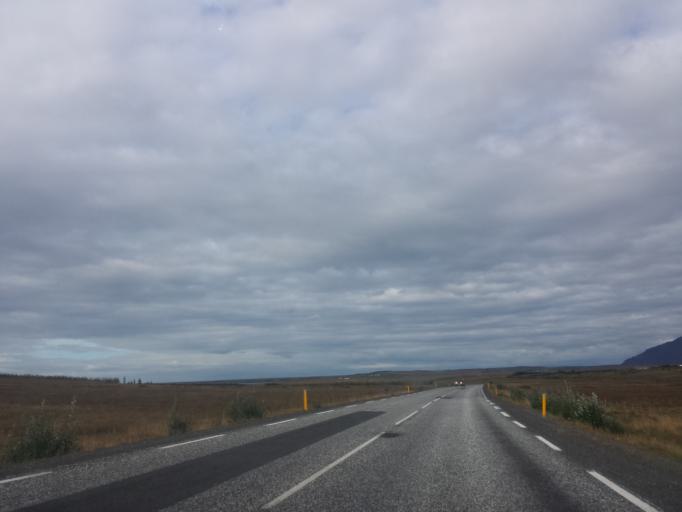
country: IS
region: West
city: Borgarnes
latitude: 64.3682
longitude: -21.8298
